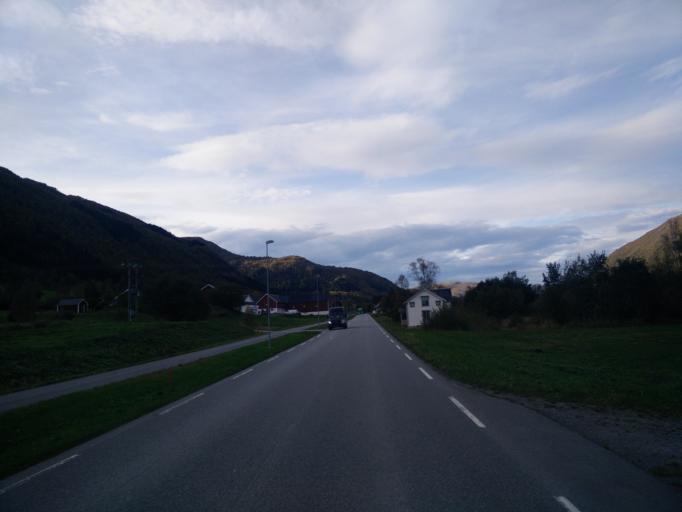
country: NO
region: More og Romsdal
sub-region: Gjemnes
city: Batnfjordsora
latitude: 62.8893
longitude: 7.6773
